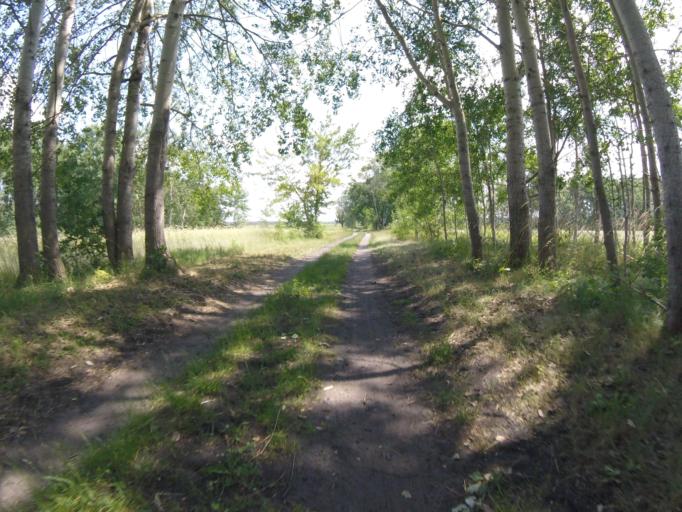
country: DE
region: Brandenburg
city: Bestensee
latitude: 52.2644
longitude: 13.7105
